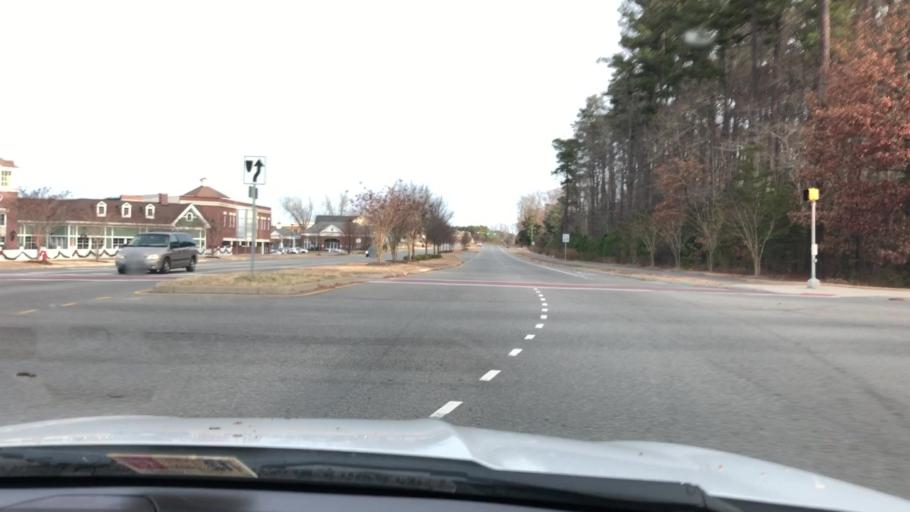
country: US
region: Virginia
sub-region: James City County
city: Williamsburg
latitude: 37.2759
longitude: -76.7385
